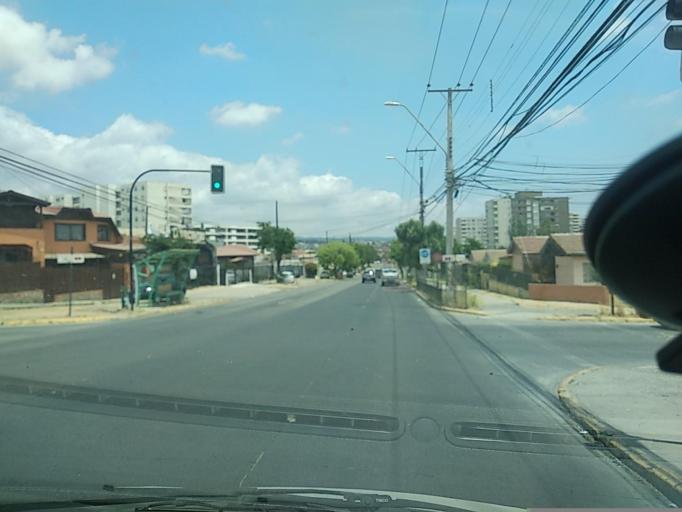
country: CL
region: Valparaiso
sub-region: Provincia de Marga Marga
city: Quilpue
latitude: -33.0425
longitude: -71.4306
